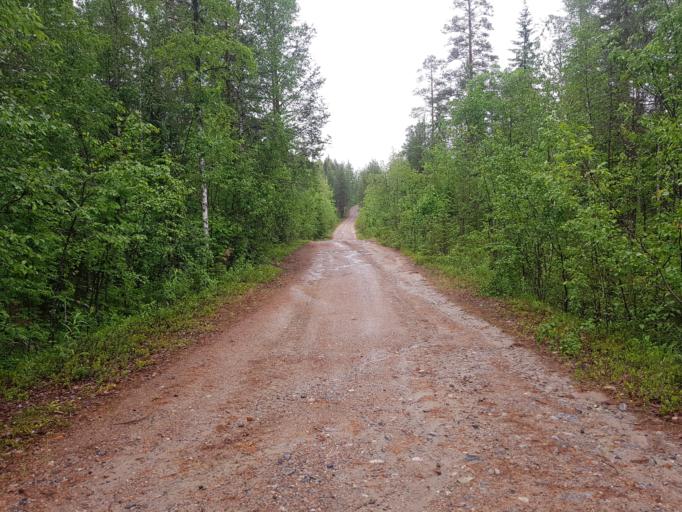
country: RU
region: Republic of Karelia
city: Kostomuksha
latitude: 64.8802
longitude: 30.2630
